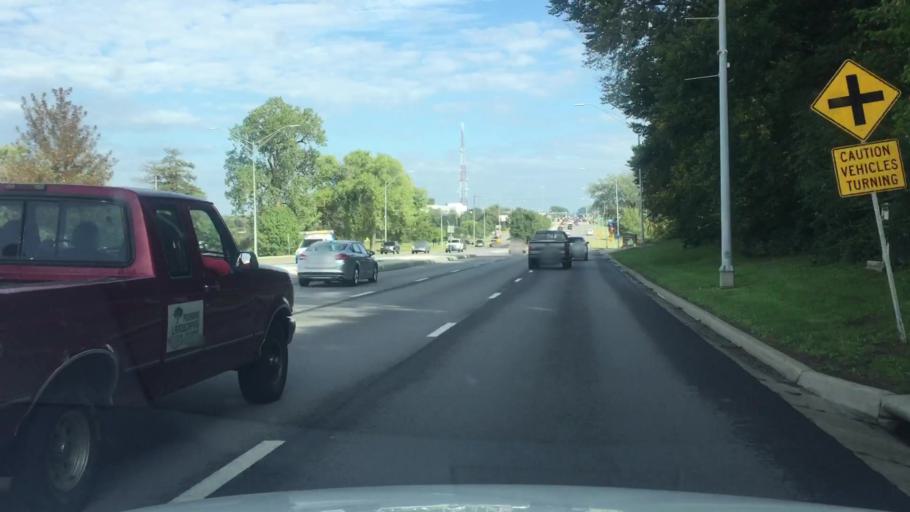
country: US
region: Kansas
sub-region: Johnson County
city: Merriam
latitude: 39.0147
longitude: -94.7023
